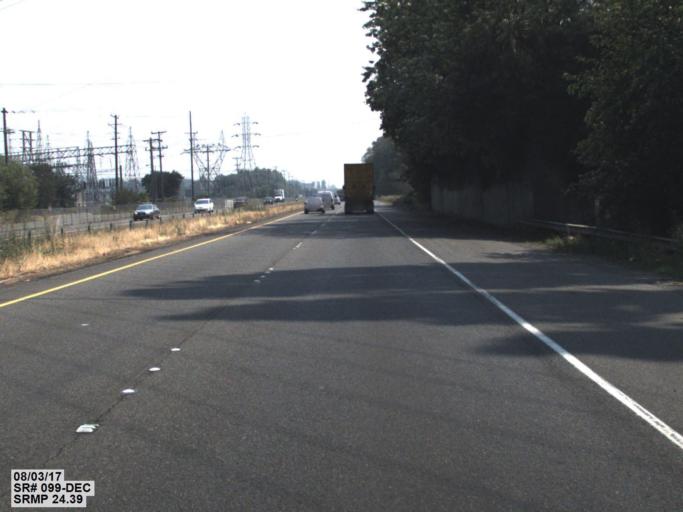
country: US
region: Washington
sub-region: King County
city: Boulevard Park
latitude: 47.5152
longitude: -122.3106
